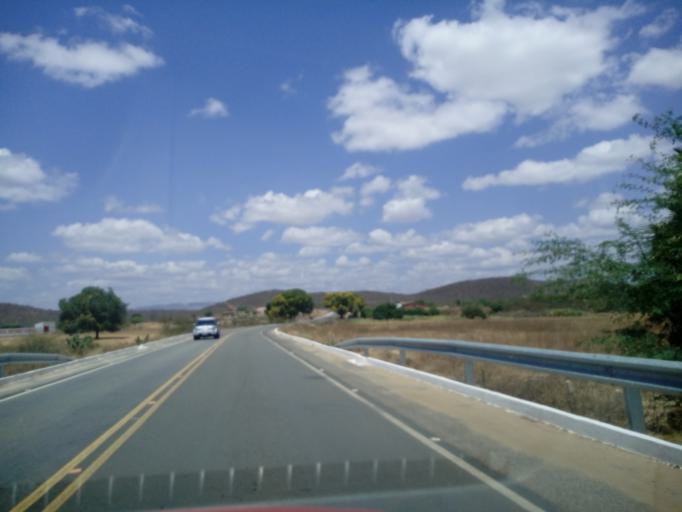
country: BR
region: Paraiba
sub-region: Patos
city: Patos
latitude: -7.0340
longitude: -37.1476
